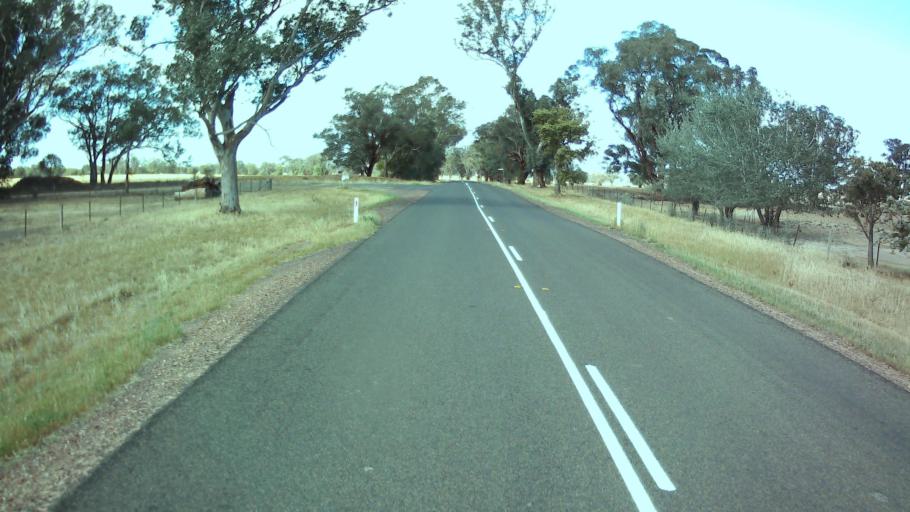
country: AU
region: New South Wales
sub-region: Weddin
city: Grenfell
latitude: -33.9659
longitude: 148.4306
